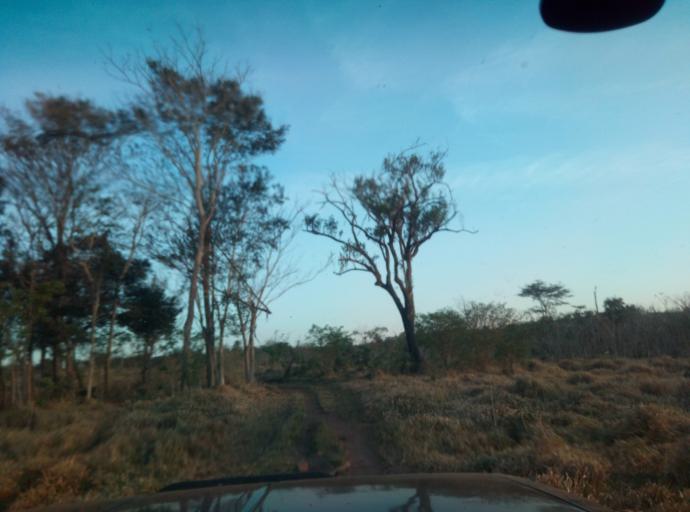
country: PY
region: Caaguazu
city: Yhu
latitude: -25.2026
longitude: -56.1081
